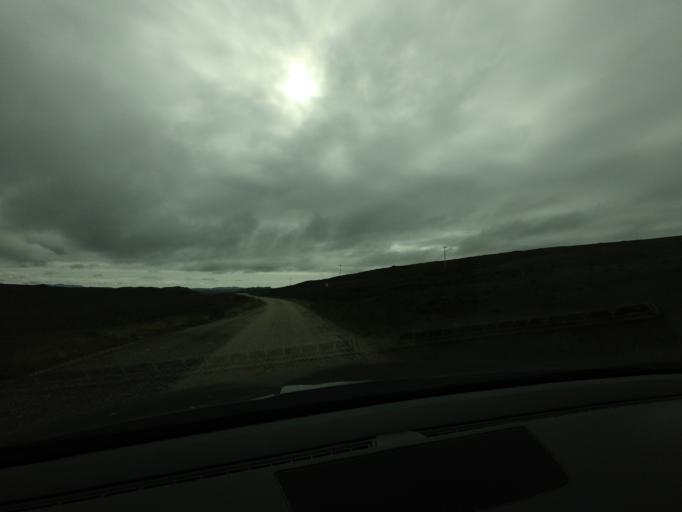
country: GB
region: Scotland
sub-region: Highland
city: Ullapool
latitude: 58.4529
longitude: -4.9331
